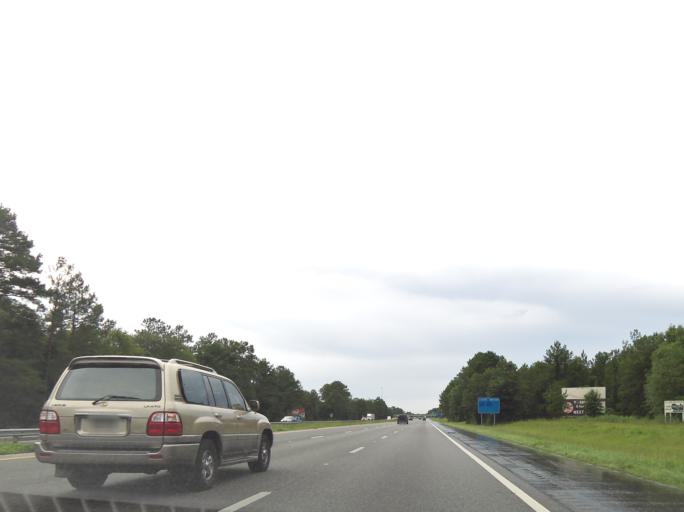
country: US
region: Georgia
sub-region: Echols County
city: Statenville
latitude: 30.5881
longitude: -83.1133
